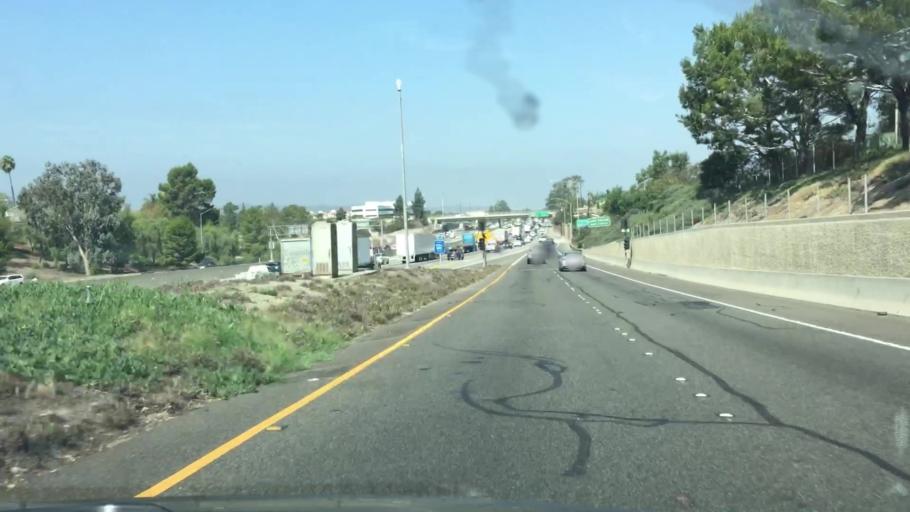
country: US
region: California
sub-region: Orange County
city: Mission Viejo
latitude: 33.6060
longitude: -117.6920
